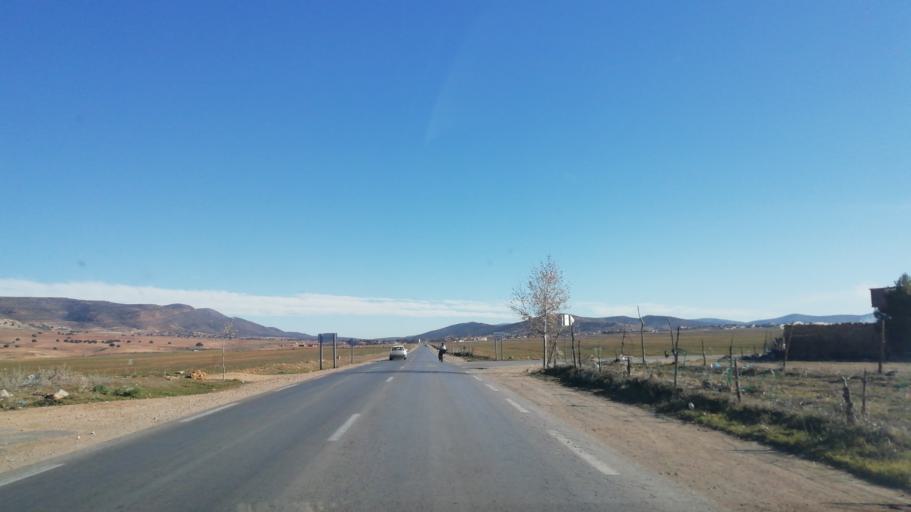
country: DZ
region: Tlemcen
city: Sebdou
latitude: 34.6654
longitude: -1.2873
